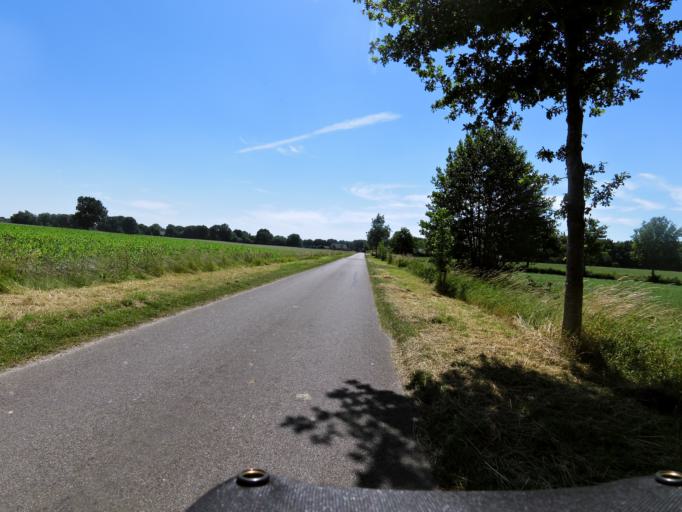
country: NL
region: Overijssel
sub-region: Gemeente Twenterand
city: Den Ham
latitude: 52.4981
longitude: 6.4030
